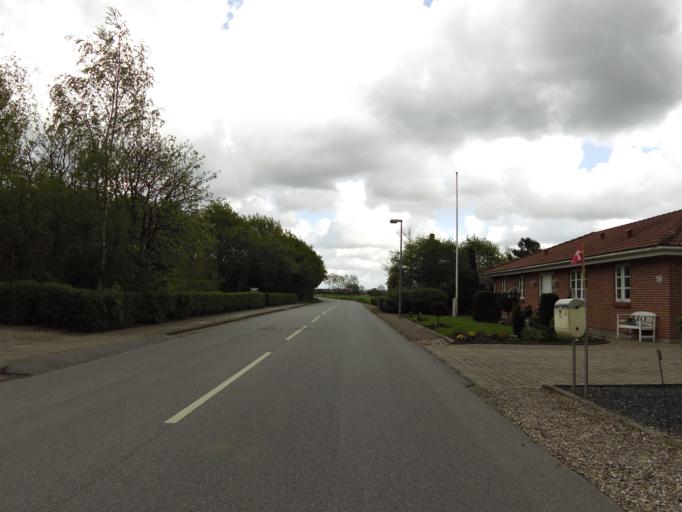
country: DK
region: South Denmark
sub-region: Haderslev Kommune
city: Gram
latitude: 55.3136
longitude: 8.9855
